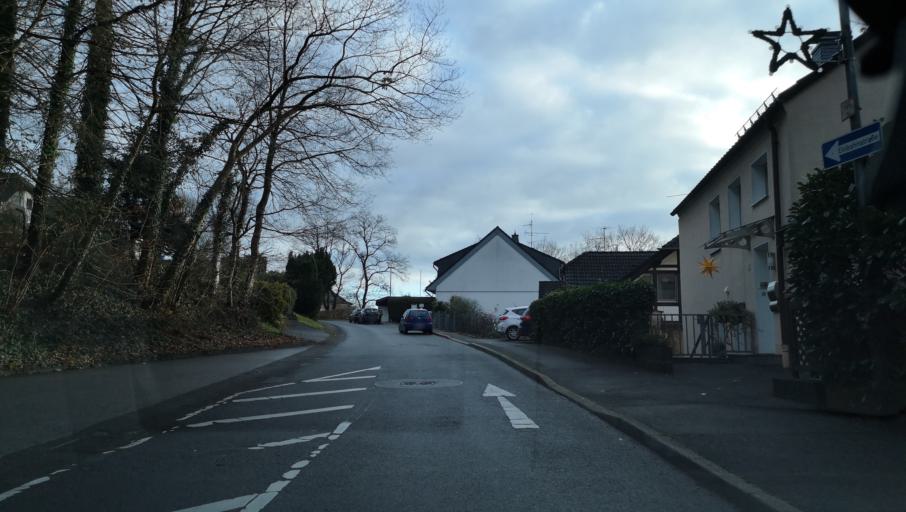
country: DE
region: North Rhine-Westphalia
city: Radevormwald
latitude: 51.2200
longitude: 7.3068
